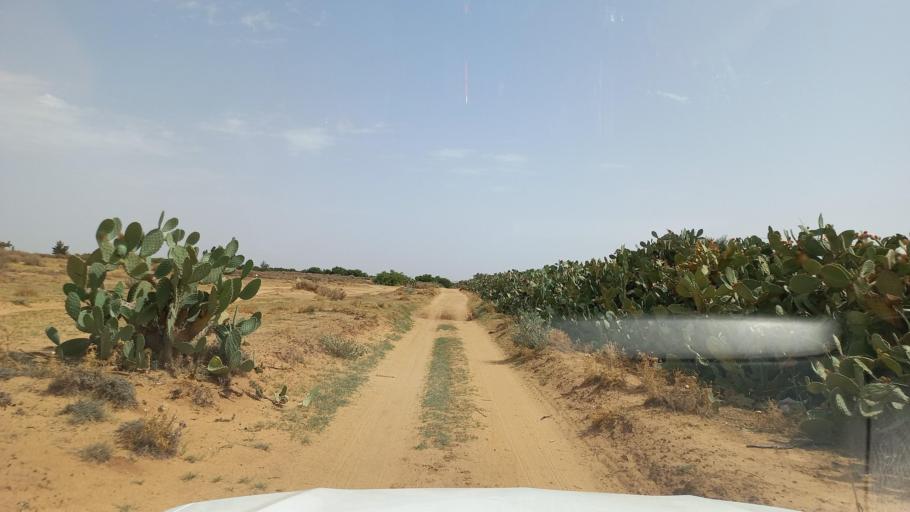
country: TN
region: Al Qasrayn
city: Kasserine
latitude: 35.2462
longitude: 9.0651
